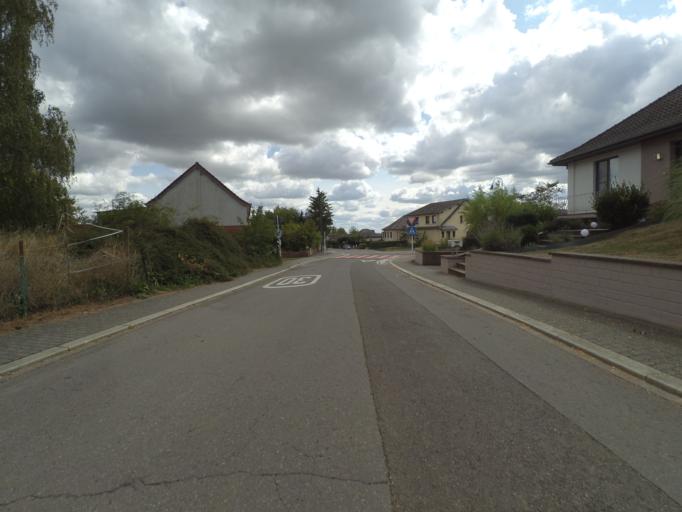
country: LU
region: Luxembourg
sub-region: Canton de Luxembourg
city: Weiler-la-Tour
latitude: 49.5547
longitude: 6.2068
